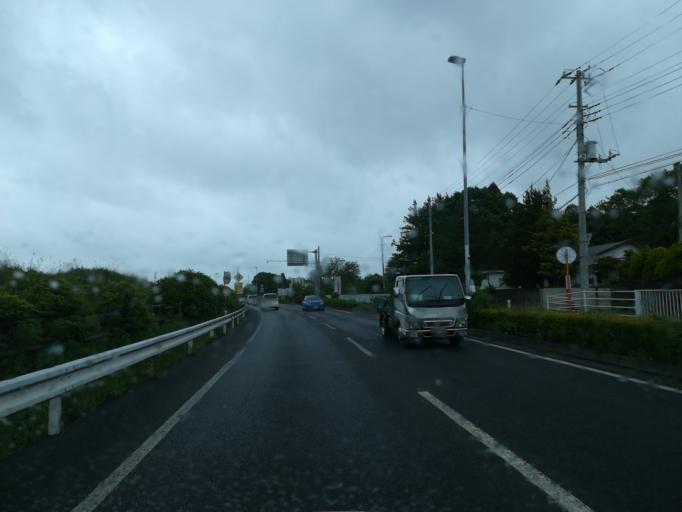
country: JP
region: Ibaraki
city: Naka
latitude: 36.0195
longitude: 140.1301
